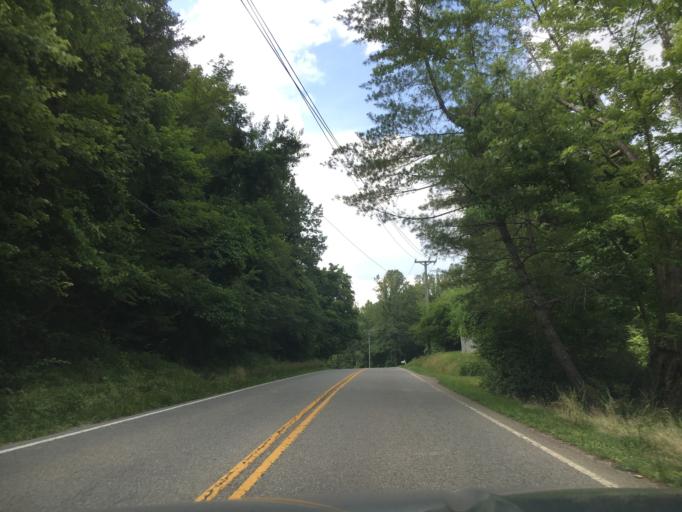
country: US
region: Virginia
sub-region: Roanoke County
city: Cave Spring
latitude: 37.1834
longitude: -80.0014
